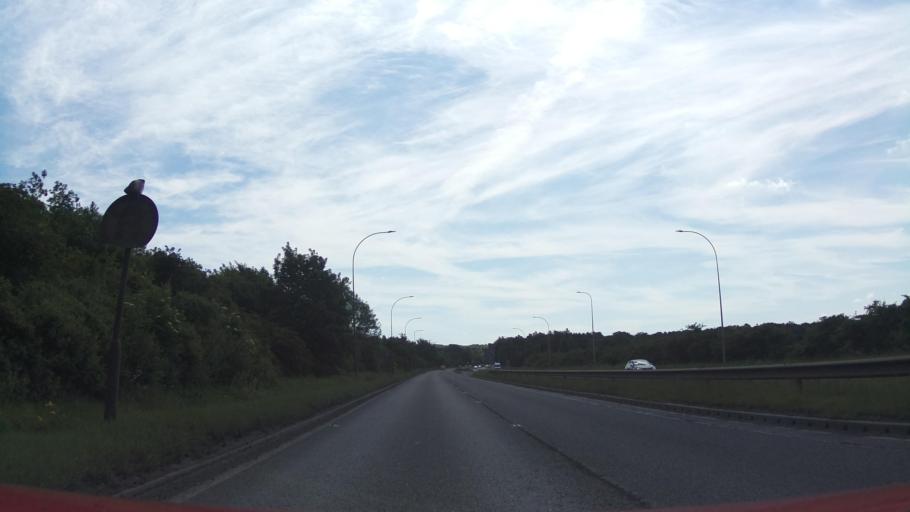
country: GB
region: England
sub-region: North Lincolnshire
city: Manton
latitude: 53.5635
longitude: -0.6041
